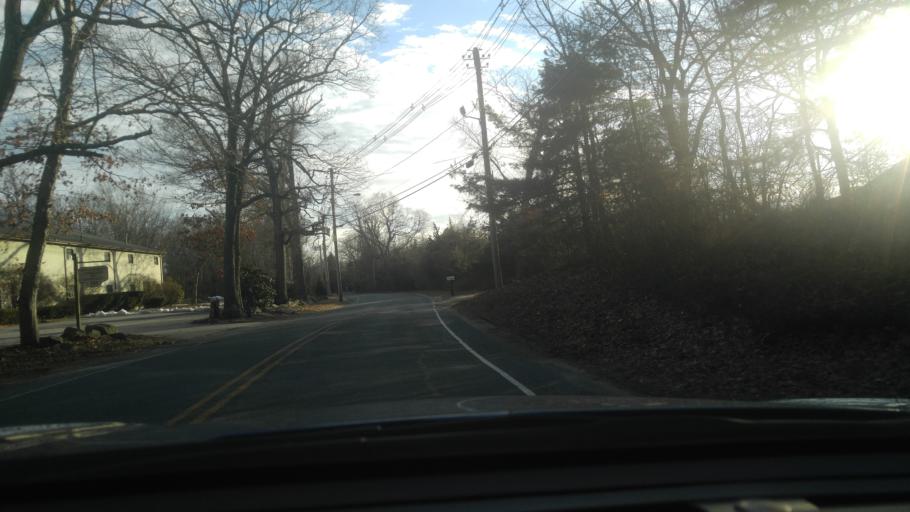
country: US
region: Rhode Island
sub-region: Kent County
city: East Greenwich
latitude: 41.6070
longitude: -71.4791
